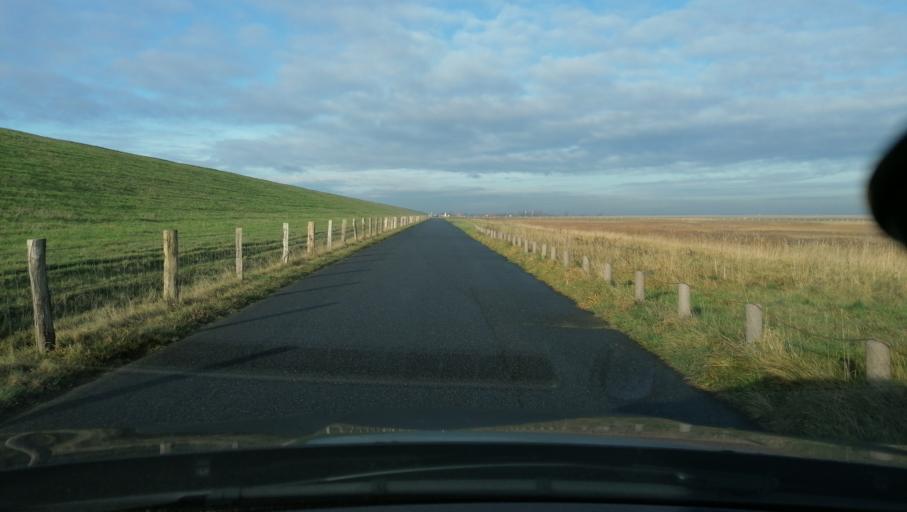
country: DE
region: Schleswig-Holstein
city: Friedrichsgabekoog
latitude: 54.0975
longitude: 8.9482
